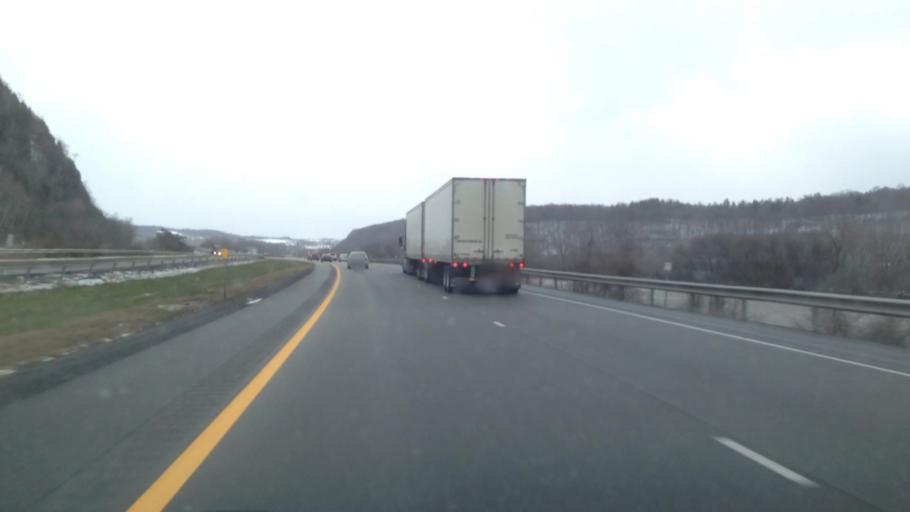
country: US
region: New York
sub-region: Montgomery County
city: Canajoharie
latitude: 42.8960
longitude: -74.4807
